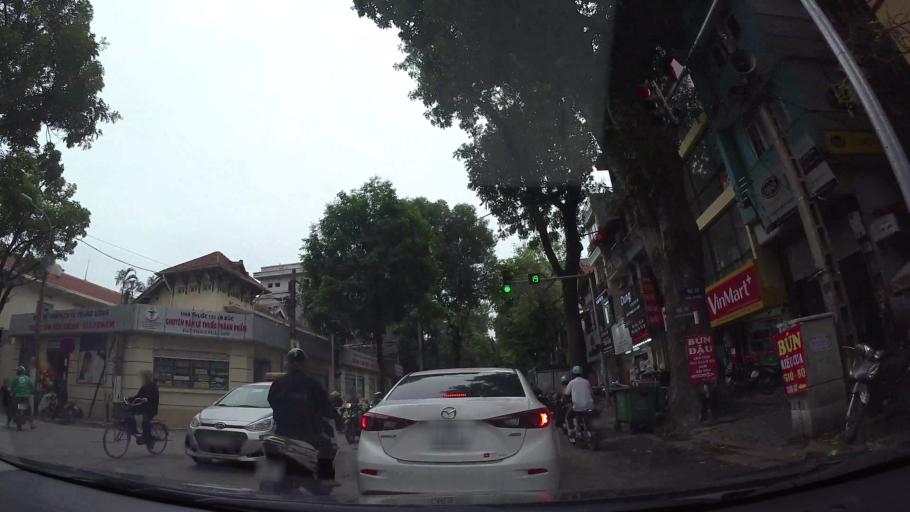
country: VN
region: Ha Noi
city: Hai BaTrung
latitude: 21.0129
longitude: 105.8583
